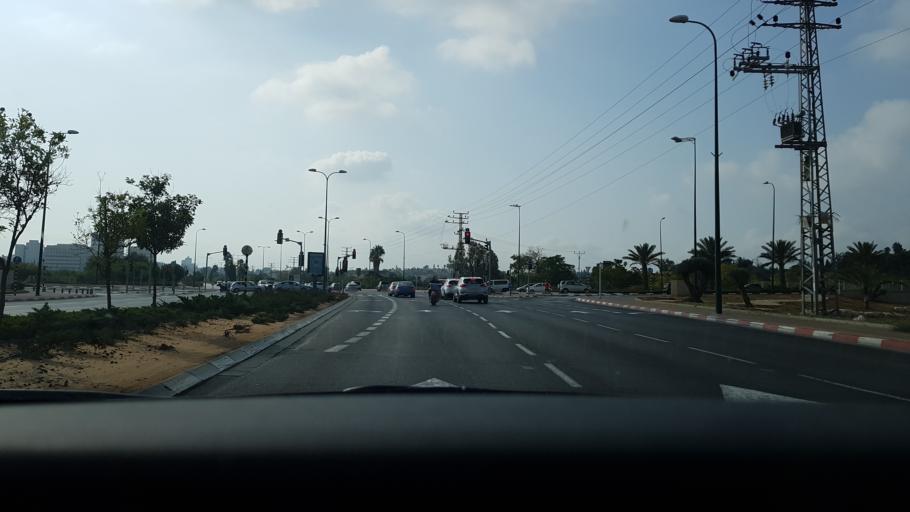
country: IL
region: Central District
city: Ness Ziona
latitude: 31.9216
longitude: 34.7979
